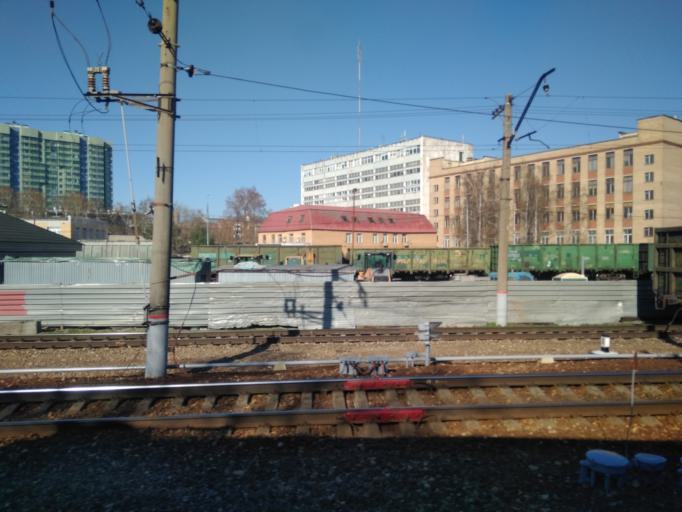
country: RU
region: Moscow
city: Pokrovskoye-Streshnevo
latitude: 55.8253
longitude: 37.4465
